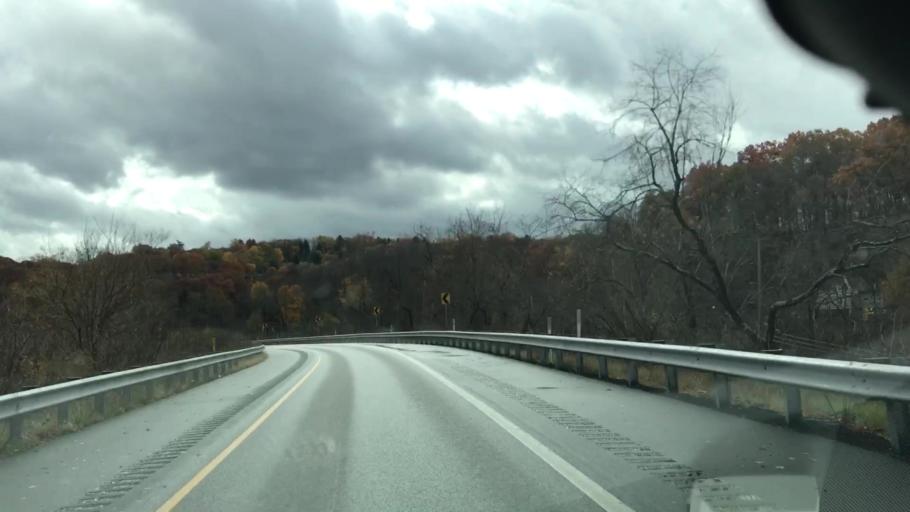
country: US
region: Pennsylvania
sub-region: Allegheny County
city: Franklin Park
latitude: 40.5890
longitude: -80.0469
